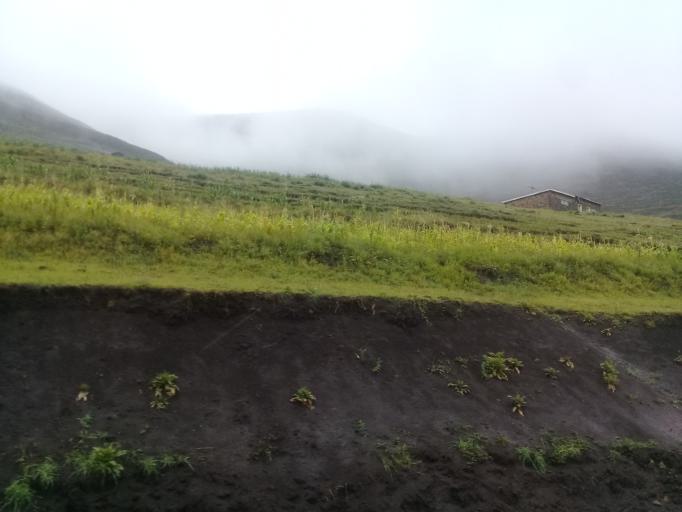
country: LS
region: Mokhotlong
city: Mokhotlong
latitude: -29.3905
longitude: 28.9652
